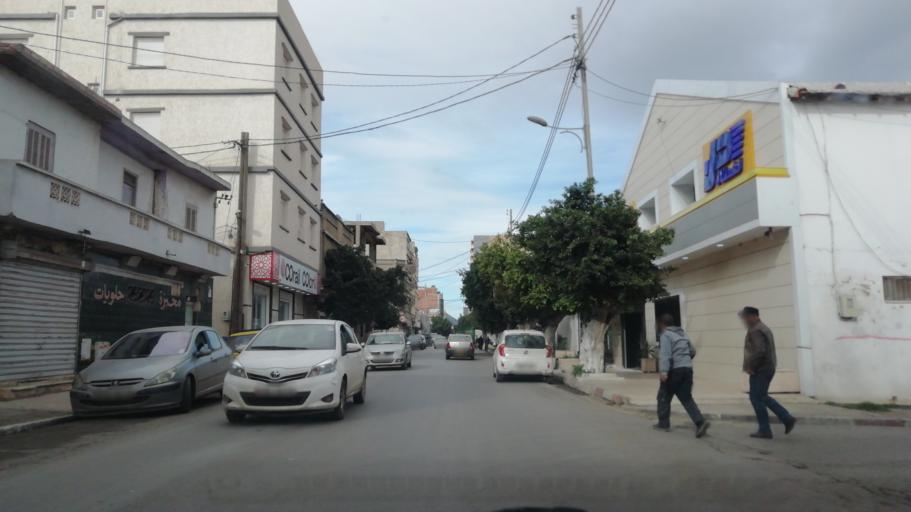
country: DZ
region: Oran
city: Oran
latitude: 35.6868
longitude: -0.6192
